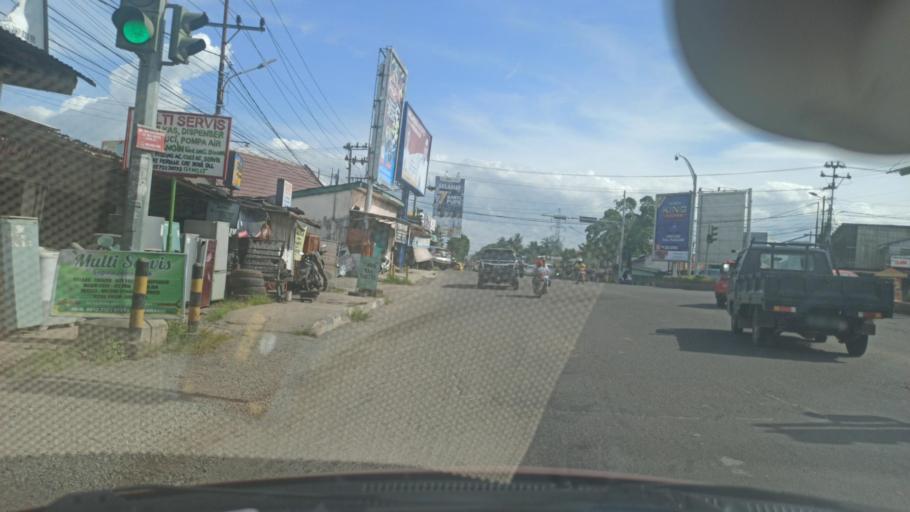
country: ID
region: South Sumatra
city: Palembang
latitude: -2.9863
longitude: 104.7250
